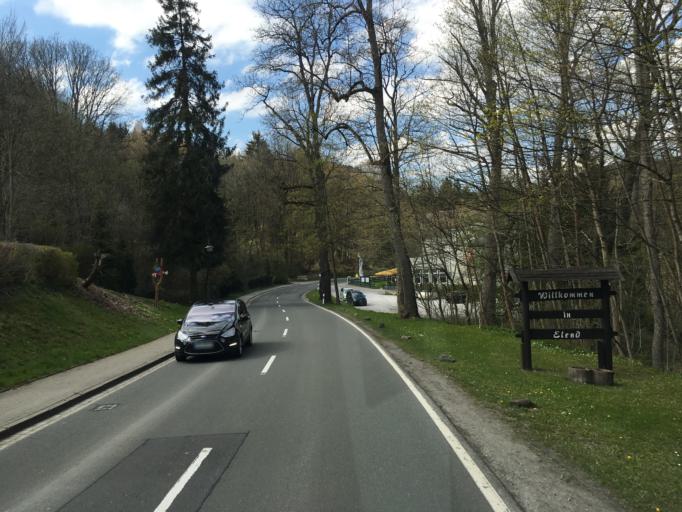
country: DE
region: Lower Saxony
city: Braunlage
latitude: 51.7427
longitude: 10.6833
